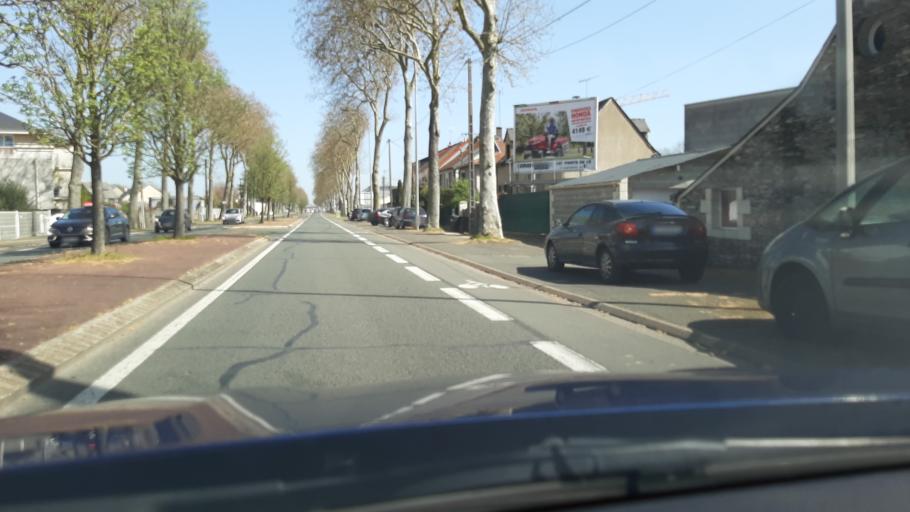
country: FR
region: Pays de la Loire
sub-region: Departement de Maine-et-Loire
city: Angers
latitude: 47.4872
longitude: -0.5124
